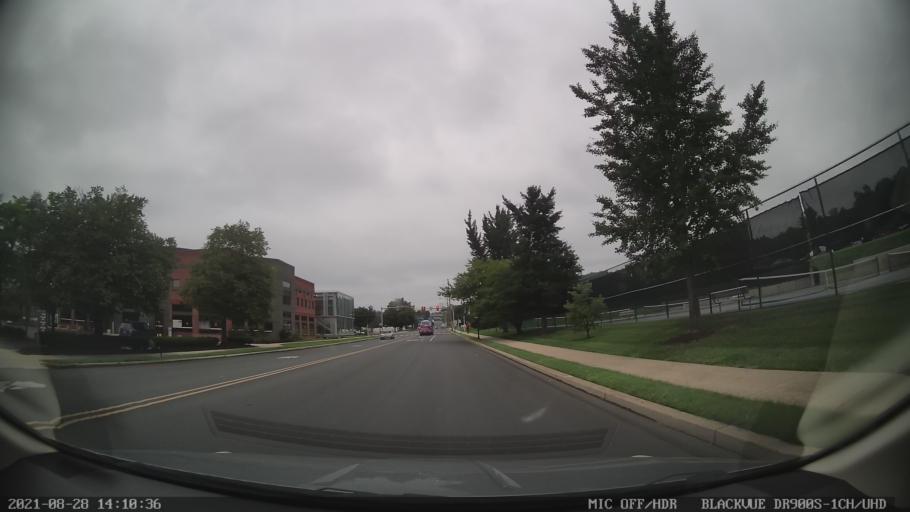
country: US
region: Pennsylvania
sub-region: Berks County
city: Hyde Park
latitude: 40.3641
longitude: -75.9114
